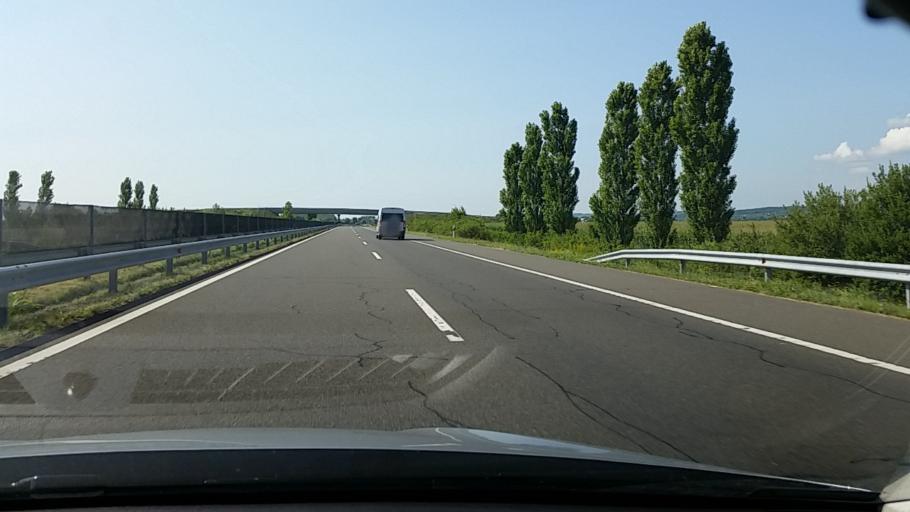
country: HU
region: Tolna
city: Decs
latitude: 46.2654
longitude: 18.7216
